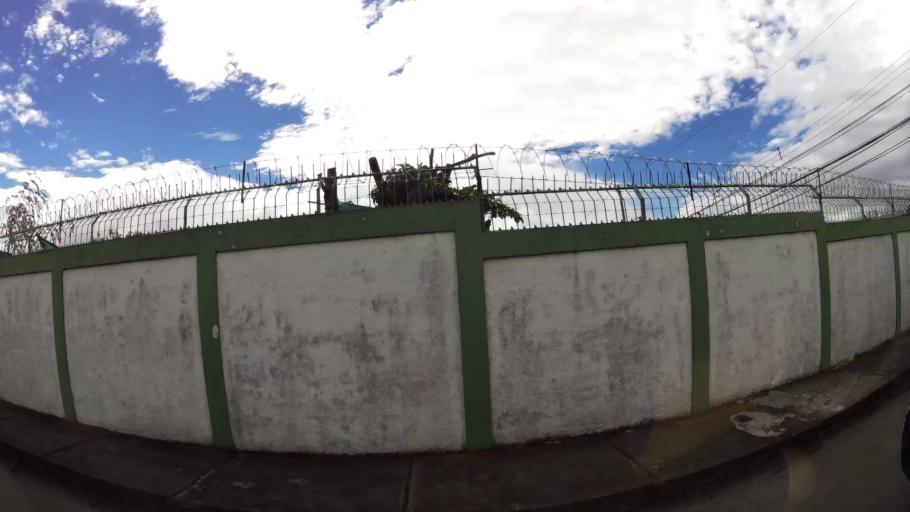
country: CR
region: Cartago
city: Tres Rios
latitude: 9.9107
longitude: -83.9853
